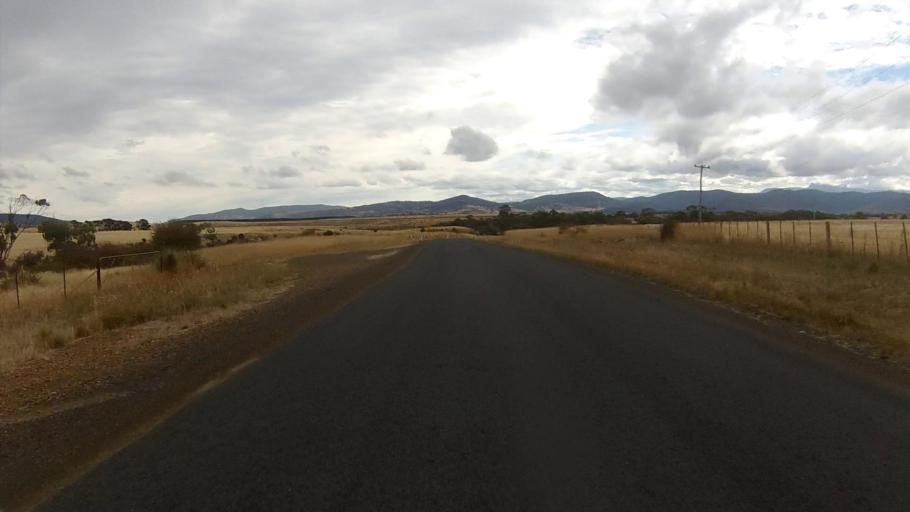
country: AU
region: Tasmania
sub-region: Northern Midlands
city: Evandale
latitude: -41.8197
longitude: 147.7562
